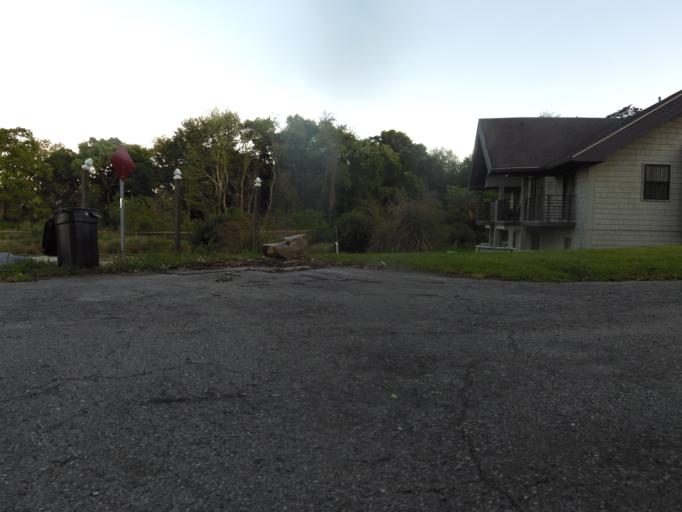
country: US
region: Florida
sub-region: Duval County
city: Jacksonville
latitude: 30.3102
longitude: -81.6320
